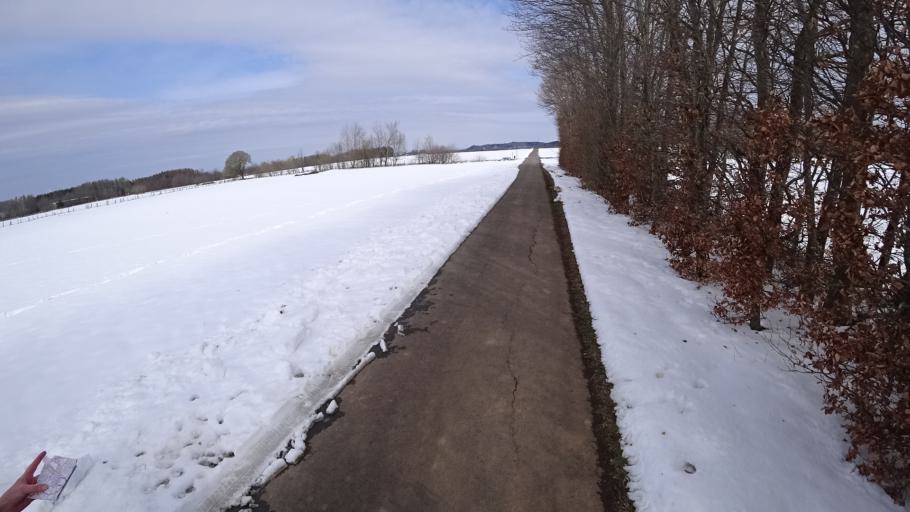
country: DE
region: Rheinland-Pfalz
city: Morlen
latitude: 50.7165
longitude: 7.8843
